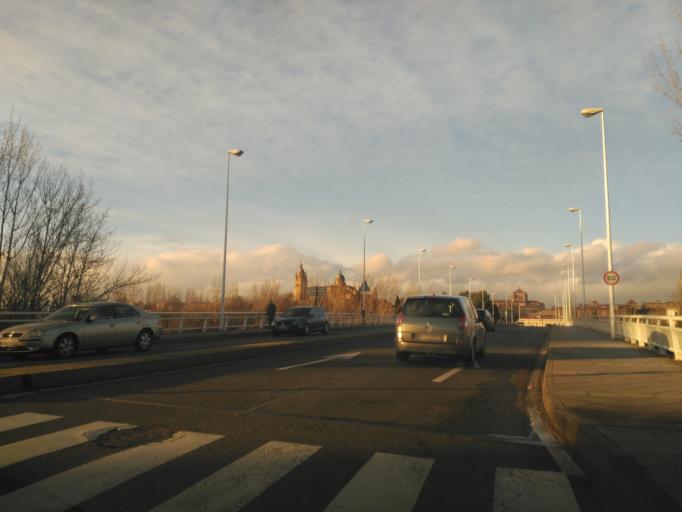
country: ES
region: Castille and Leon
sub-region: Provincia de Salamanca
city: Salamanca
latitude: 40.9528
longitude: -5.6615
